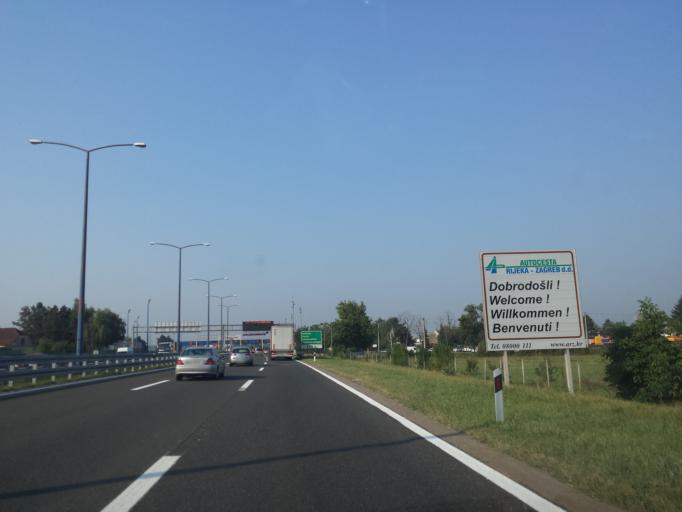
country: HR
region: Grad Zagreb
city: Brezovica
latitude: 45.7516
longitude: 15.8866
